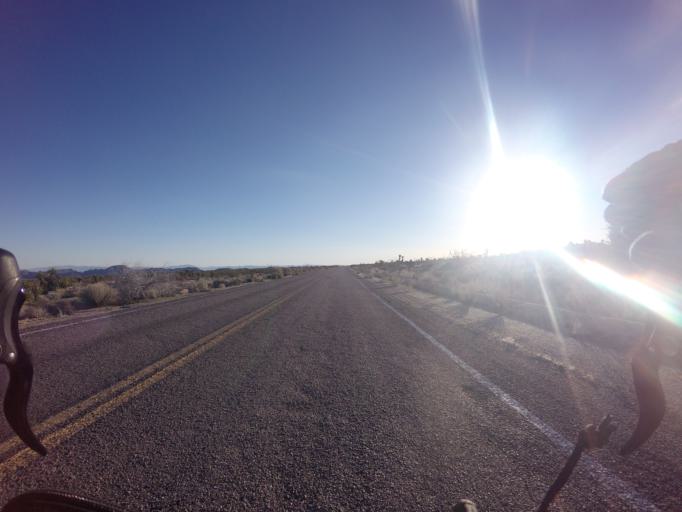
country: US
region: California
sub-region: San Bernardino County
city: Twentynine Palms
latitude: 34.7723
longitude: -115.6286
